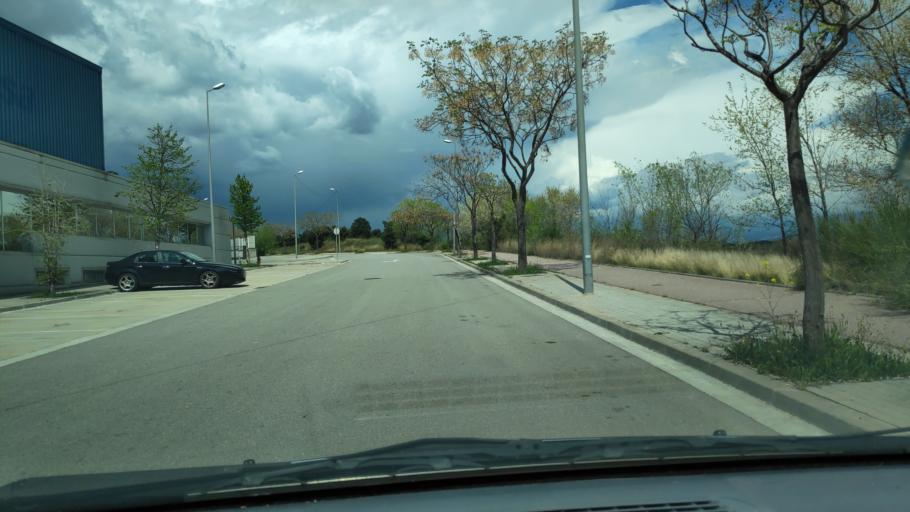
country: ES
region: Catalonia
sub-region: Provincia de Barcelona
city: Polinya
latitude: 41.5384
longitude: 2.1395
